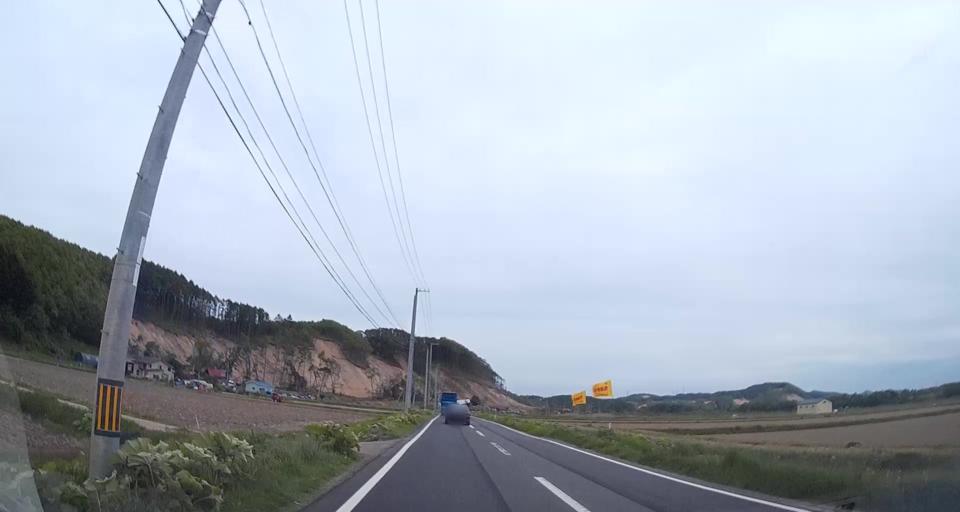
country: JP
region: Hokkaido
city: Chitose
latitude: 42.7465
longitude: 141.9082
